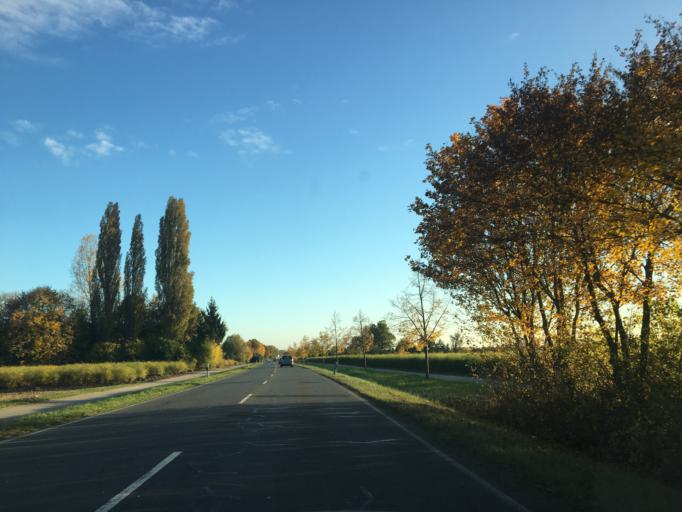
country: DE
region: Hesse
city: Zwingenberg
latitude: 49.7153
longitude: 8.6048
